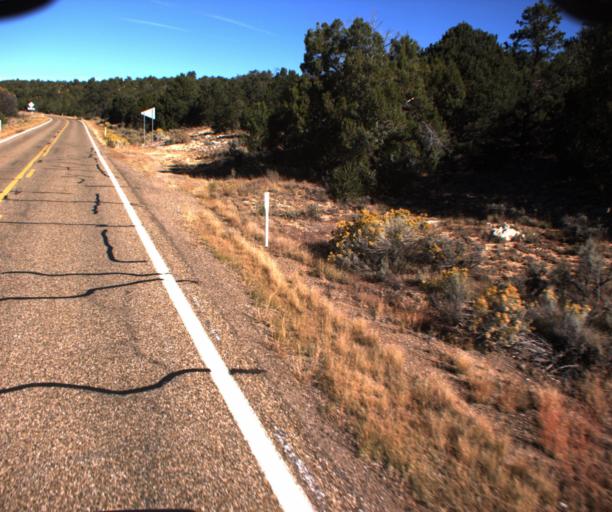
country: US
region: Arizona
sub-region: Coconino County
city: Fredonia
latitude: 36.7348
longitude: -112.0978
